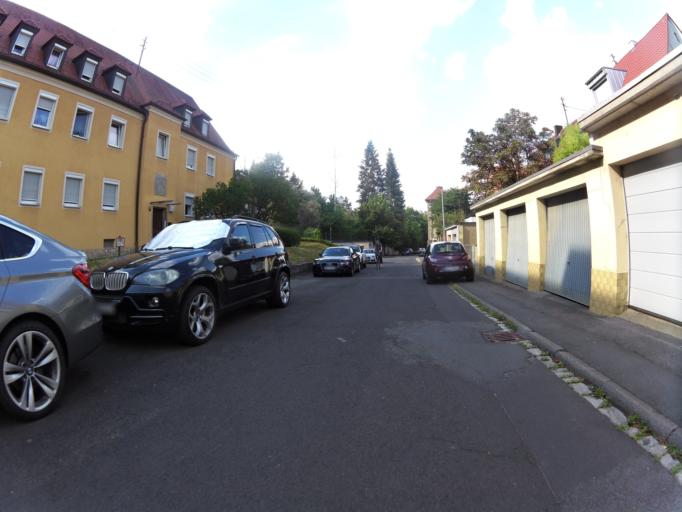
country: DE
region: Bavaria
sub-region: Regierungsbezirk Unterfranken
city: Ochsenfurt
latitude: 49.6615
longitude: 10.0594
